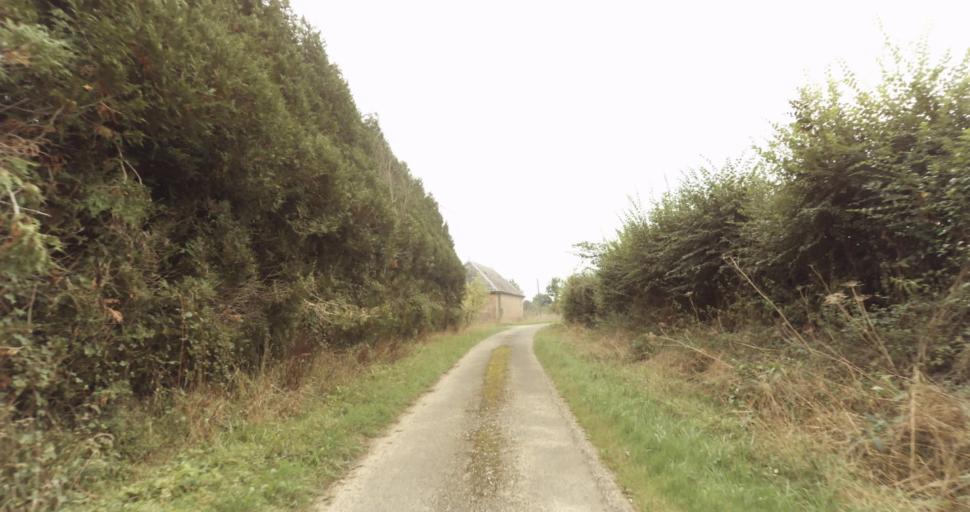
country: FR
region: Lower Normandy
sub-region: Departement de l'Orne
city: Gace
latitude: 48.7702
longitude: 0.3019
